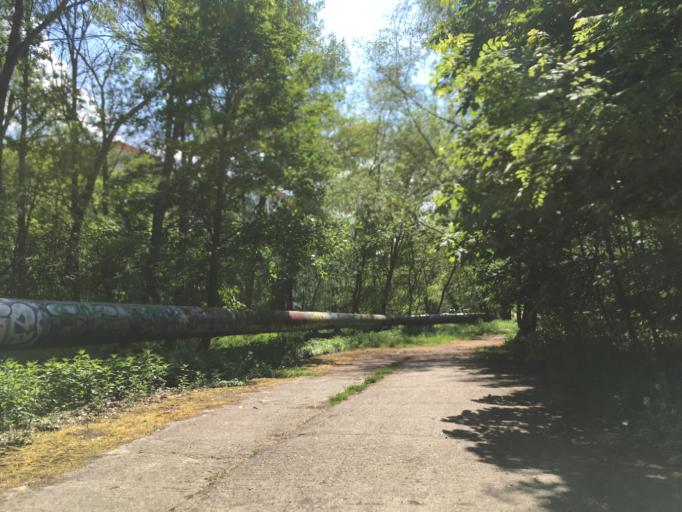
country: DE
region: Berlin
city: Neu-Hohenschoenhausen
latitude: 52.5754
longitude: 13.4978
